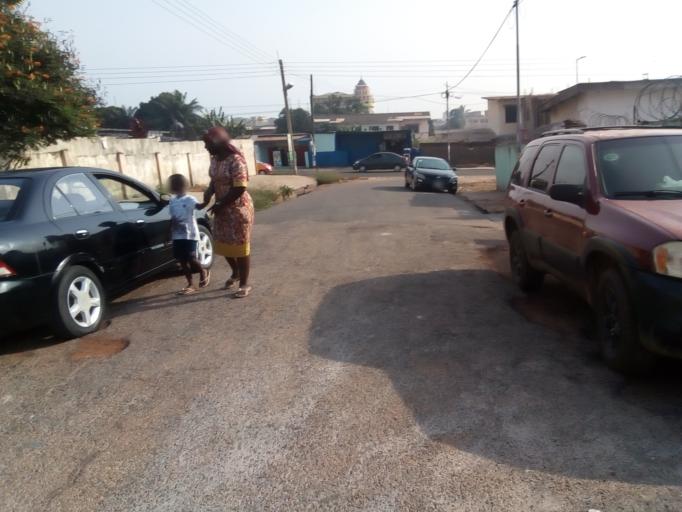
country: GH
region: Greater Accra
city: Accra
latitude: 5.5856
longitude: -0.2143
